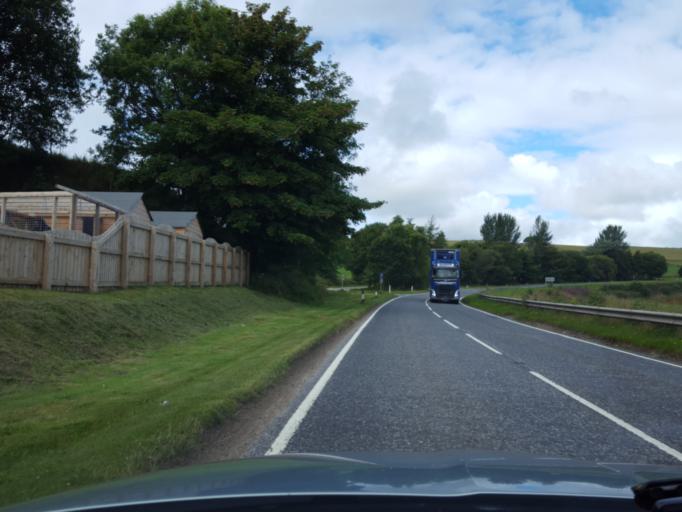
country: GB
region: Scotland
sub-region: Moray
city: Rothes
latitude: 57.5351
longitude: -3.2195
